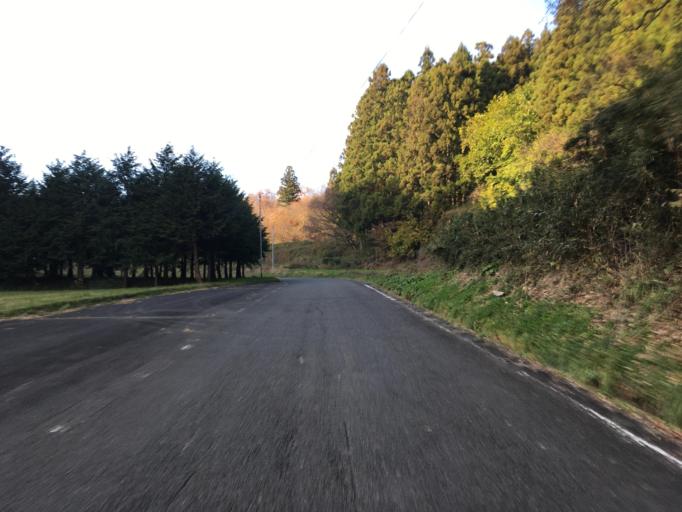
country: JP
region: Fukushima
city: Ishikawa
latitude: 37.2448
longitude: 140.5862
